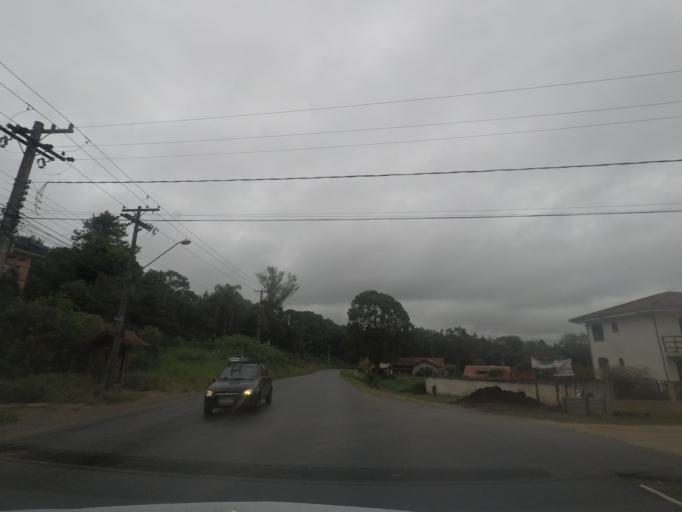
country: BR
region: Parana
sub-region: Quatro Barras
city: Quatro Barras
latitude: -25.3878
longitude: -49.1402
